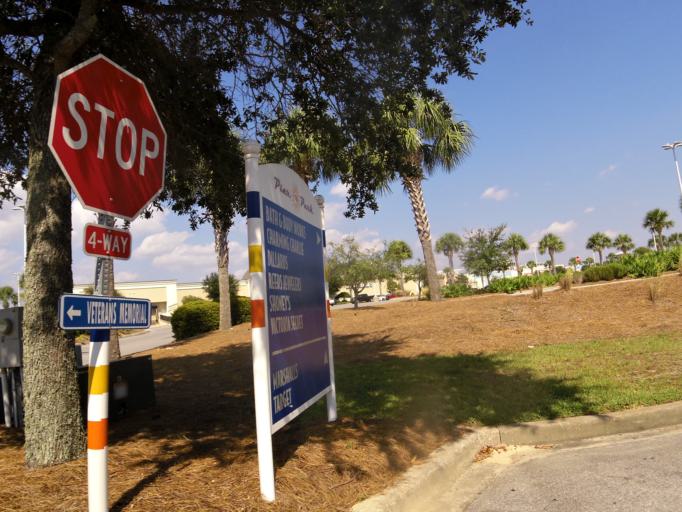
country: US
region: Florida
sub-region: Bay County
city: Laguna Beach
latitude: 30.2203
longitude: -85.8730
